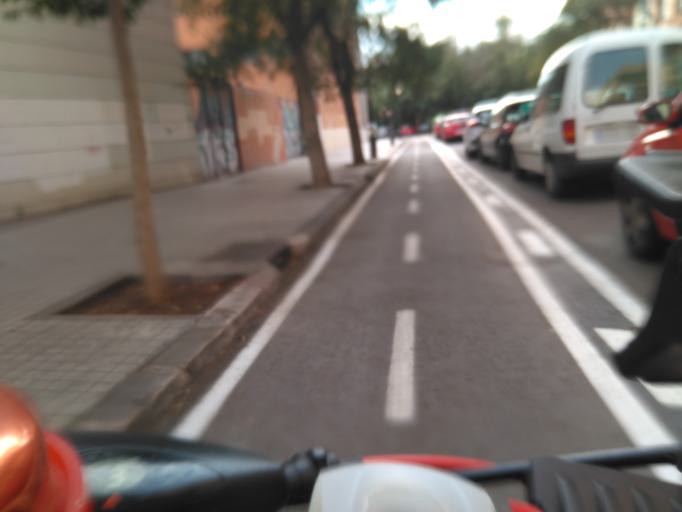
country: ES
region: Valencia
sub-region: Provincia de Valencia
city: Valencia
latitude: 39.4829
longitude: -0.3695
